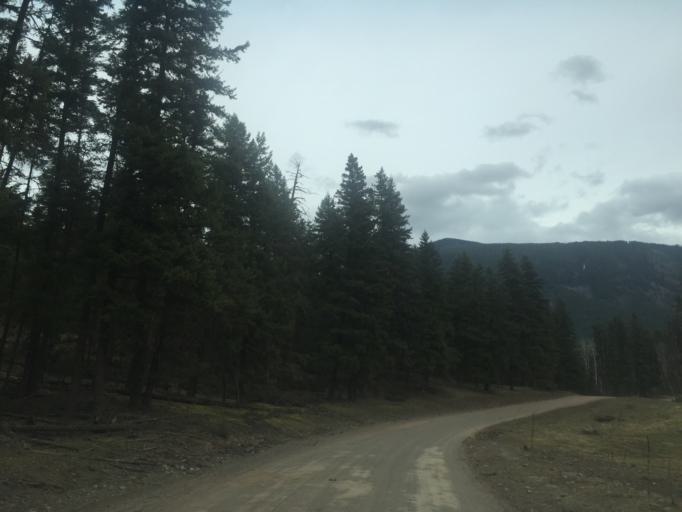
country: CA
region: British Columbia
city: Chase
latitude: 51.3745
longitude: -120.1504
